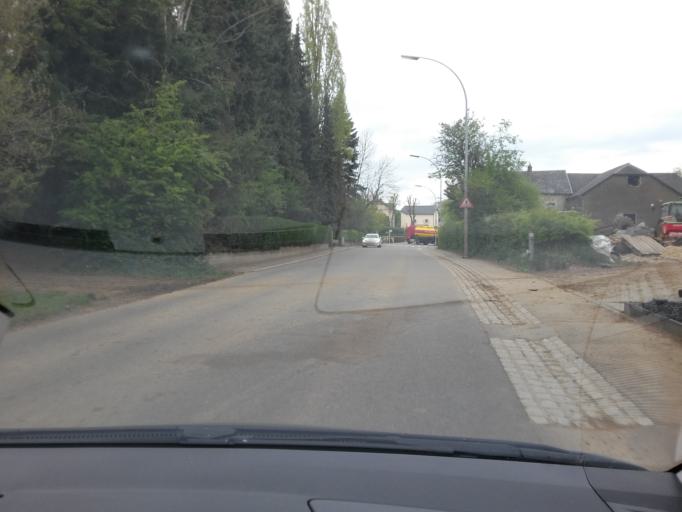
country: LU
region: Luxembourg
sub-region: Canton de Capellen
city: Garnich
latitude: 49.6027
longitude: 5.9282
